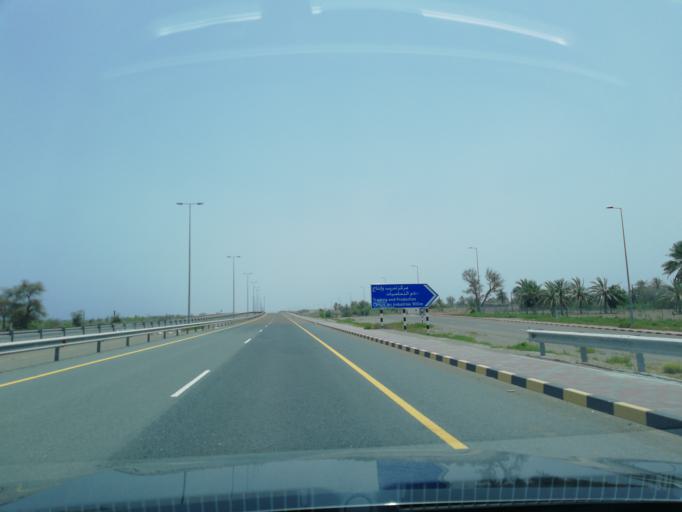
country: OM
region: Al Batinah
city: Shinas
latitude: 24.7712
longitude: 56.4590
